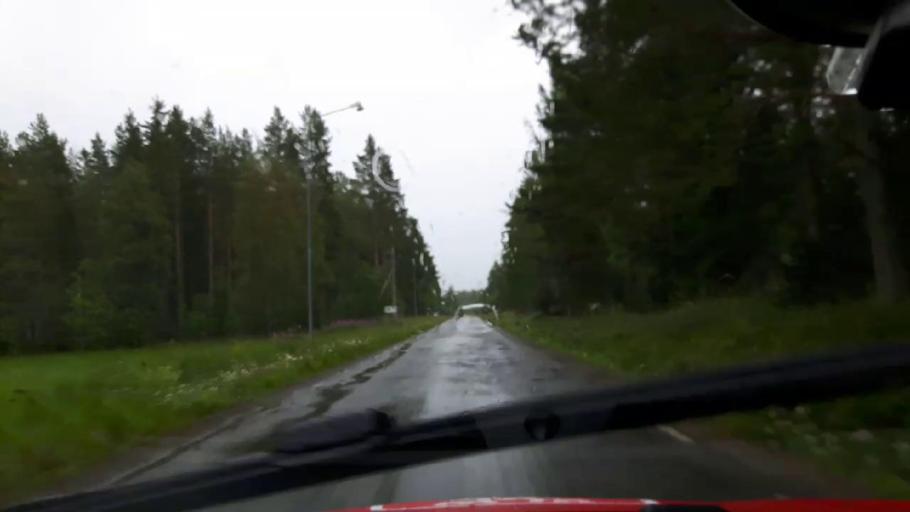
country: SE
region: Jaemtland
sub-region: OEstersunds Kommun
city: Brunflo
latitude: 62.9829
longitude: 14.8198
